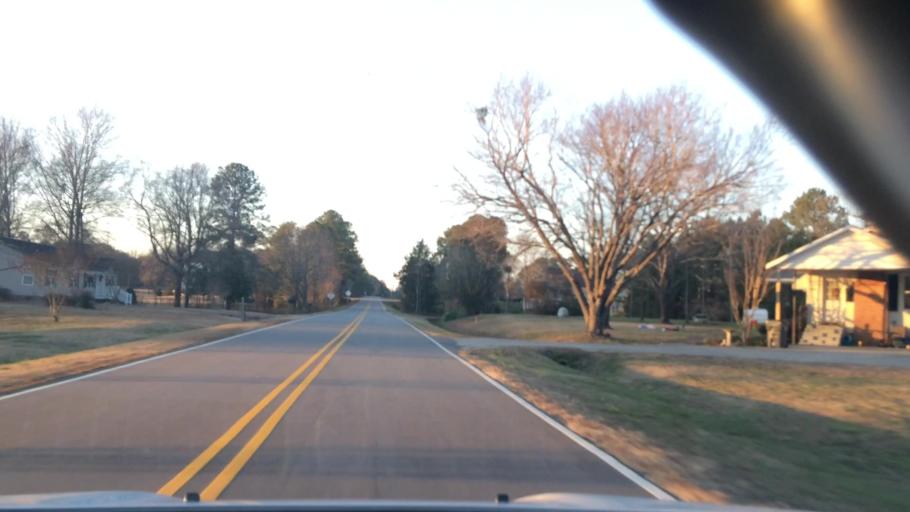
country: US
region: North Carolina
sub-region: Wake County
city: Rolesville
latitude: 35.9426
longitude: -78.4045
